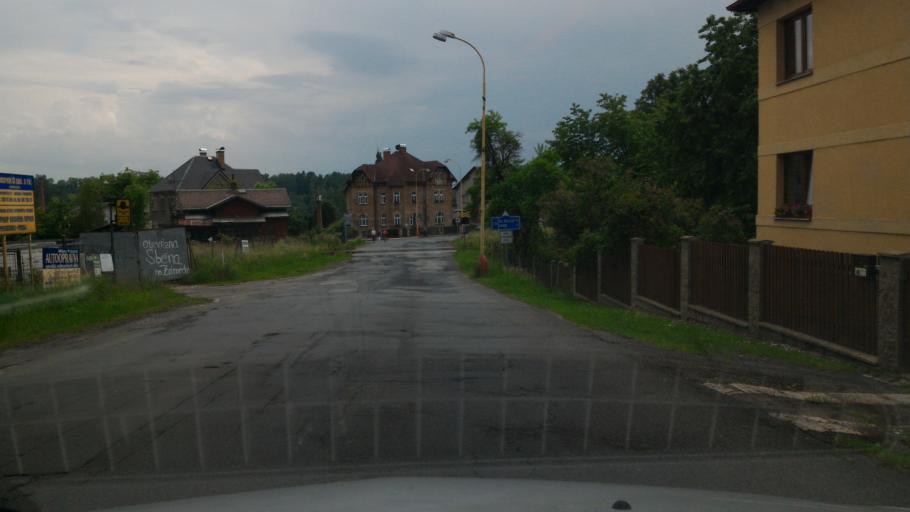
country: CZ
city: Jablonne v Podjestedi
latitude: 50.7705
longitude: 14.7679
